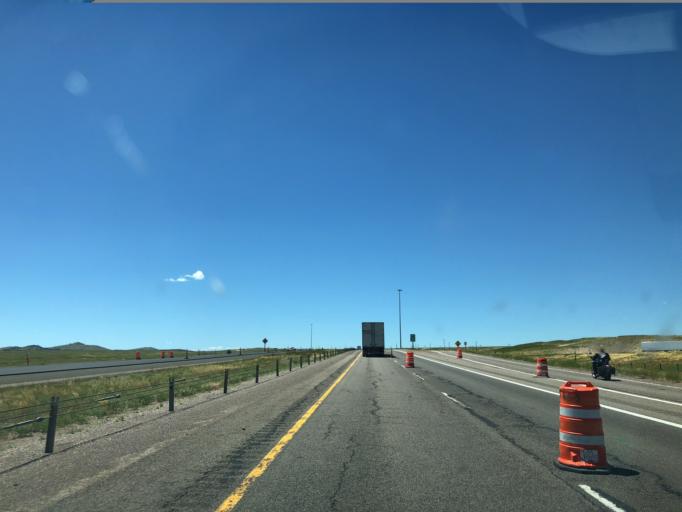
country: US
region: Wyoming
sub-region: Laramie County
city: Cheyenne
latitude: 41.0979
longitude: -105.1120
